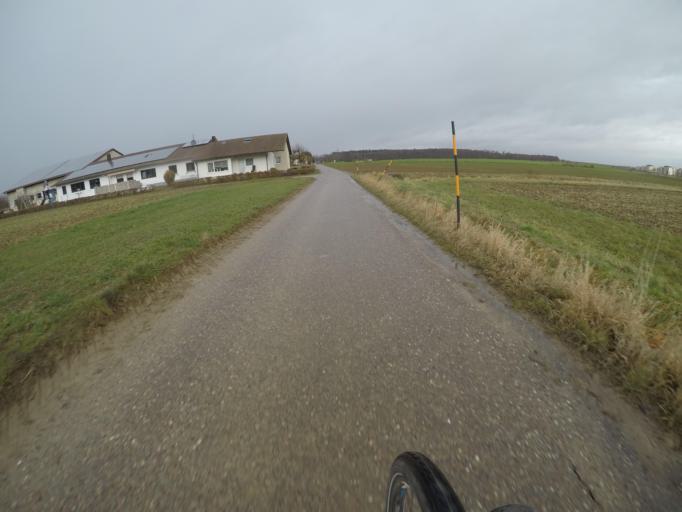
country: DE
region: Baden-Wuerttemberg
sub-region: Regierungsbezirk Stuttgart
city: Hemmingen
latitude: 48.8632
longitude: 9.0120
